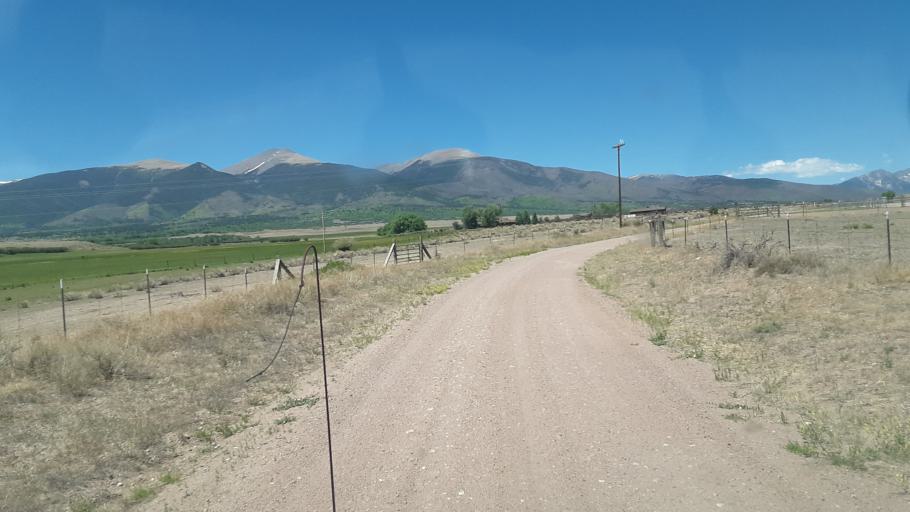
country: US
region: Colorado
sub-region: Custer County
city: Westcliffe
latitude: 38.2921
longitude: -105.6225
